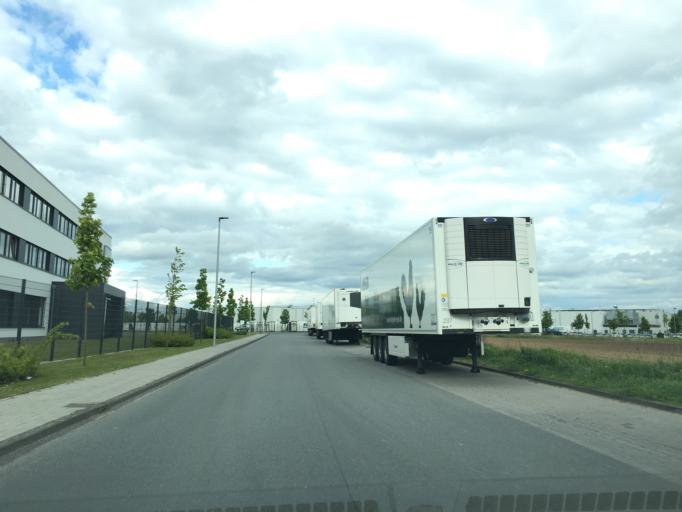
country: DE
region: North Rhine-Westphalia
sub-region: Regierungsbezirk Munster
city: Muenster
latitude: 52.0096
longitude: 7.6714
